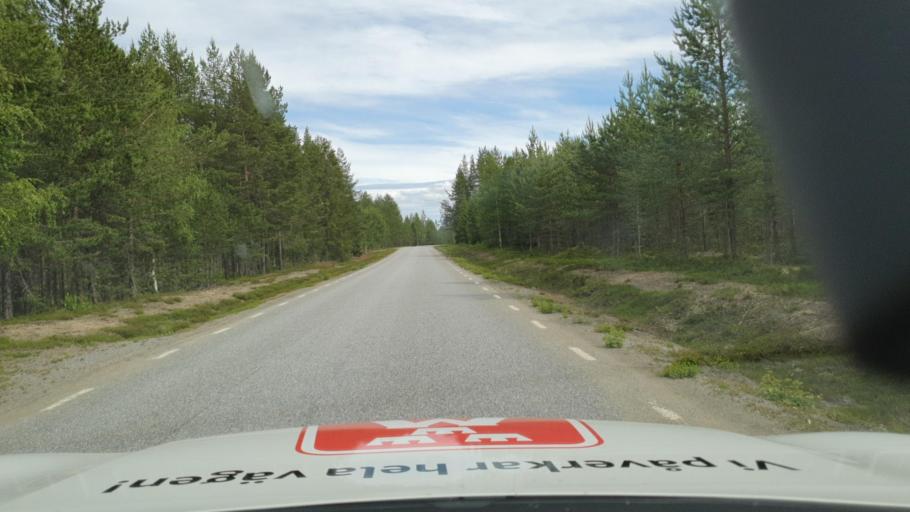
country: SE
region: Vaesterbotten
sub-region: Skelleftea Kommun
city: Burtraesk
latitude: 64.5031
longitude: 20.8293
